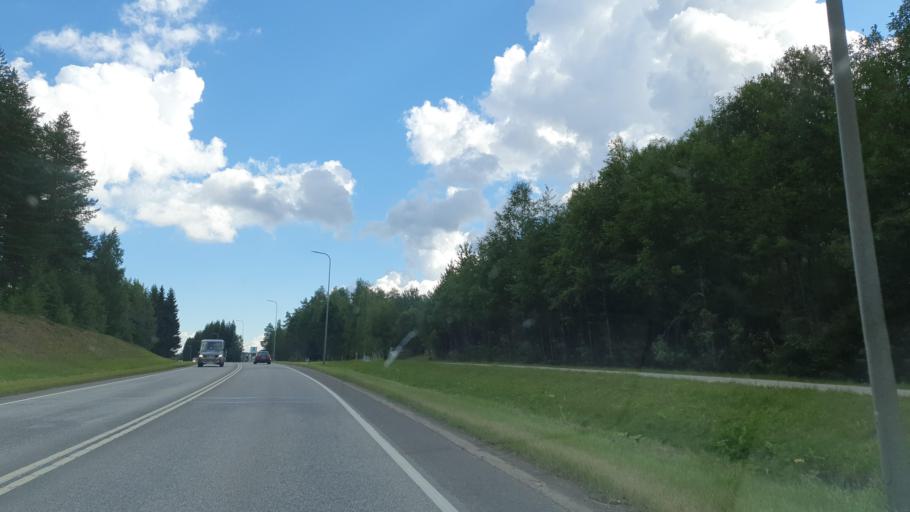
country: FI
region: Kainuu
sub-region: Kajaani
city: Kajaani
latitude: 64.2172
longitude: 27.7023
